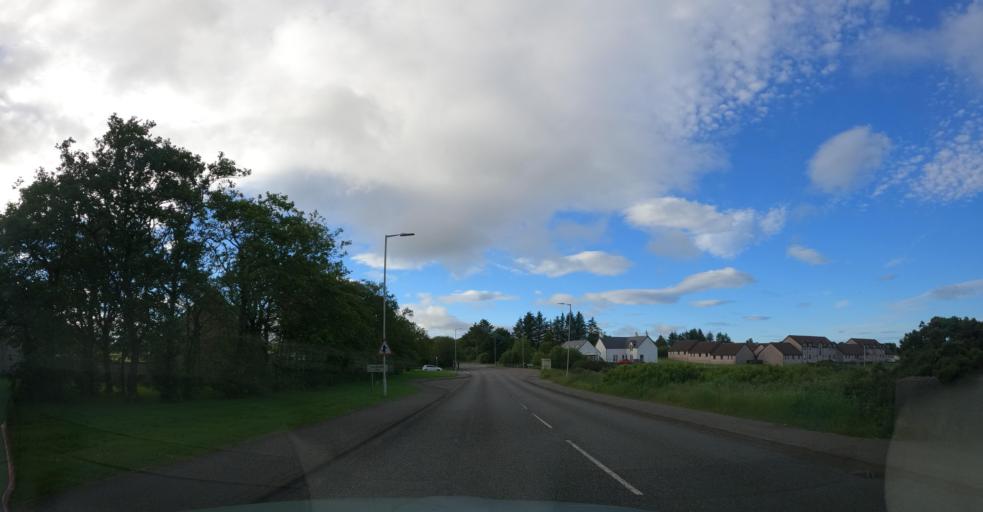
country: GB
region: Scotland
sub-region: Eilean Siar
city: Isle of Lewis
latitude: 58.2232
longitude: -6.3860
